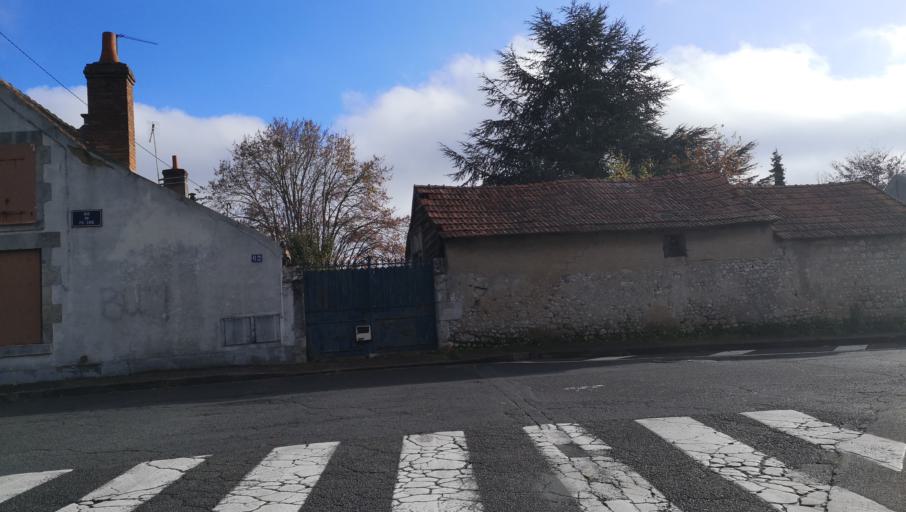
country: FR
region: Centre
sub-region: Departement du Loiret
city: Fleury-les-Aubrais
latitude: 47.9199
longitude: 1.9309
